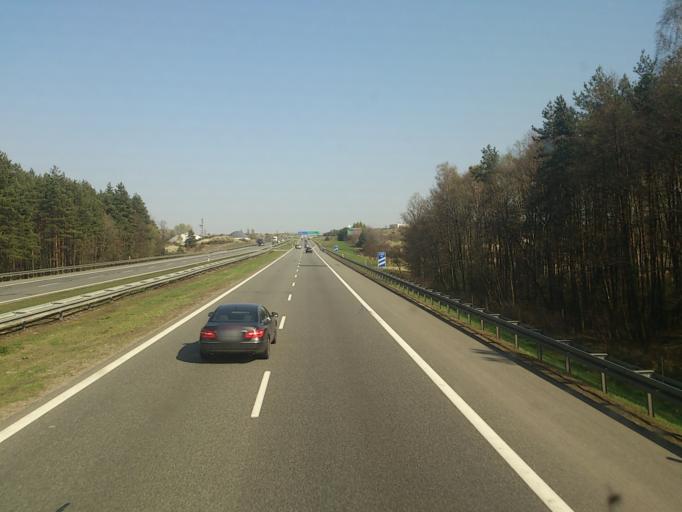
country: PL
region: Lesser Poland Voivodeship
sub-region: Powiat chrzanowski
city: Regulice
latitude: 50.1027
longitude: 19.5374
